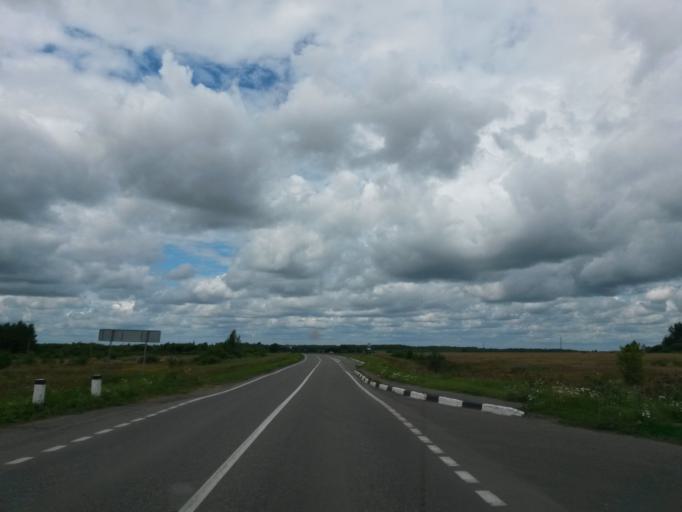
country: RU
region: Jaroslavl
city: Konstantinovskiy
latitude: 57.8699
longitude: 39.5982
